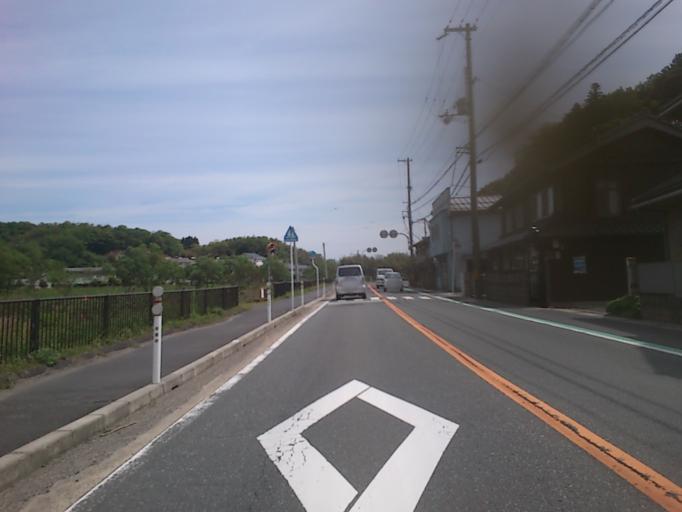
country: JP
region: Kyoto
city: Miyazu
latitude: 35.6378
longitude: 135.0800
